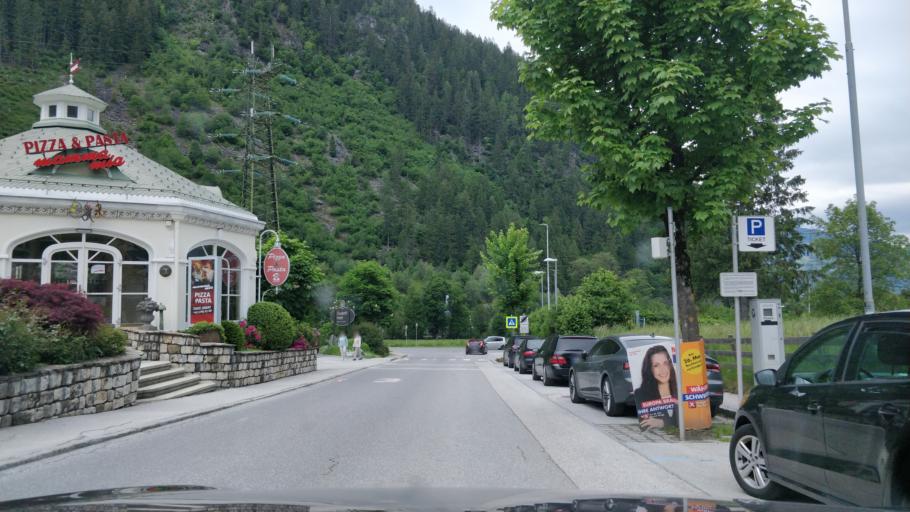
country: AT
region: Tyrol
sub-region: Politischer Bezirk Schwaz
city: Mayrhofen
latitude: 47.1676
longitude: 11.8616
